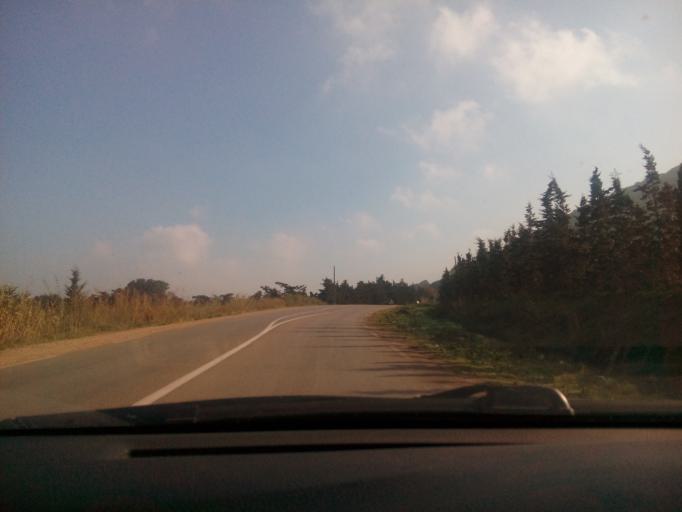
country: DZ
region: Oran
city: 'Ain el Turk
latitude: 35.7041
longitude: -0.8400
